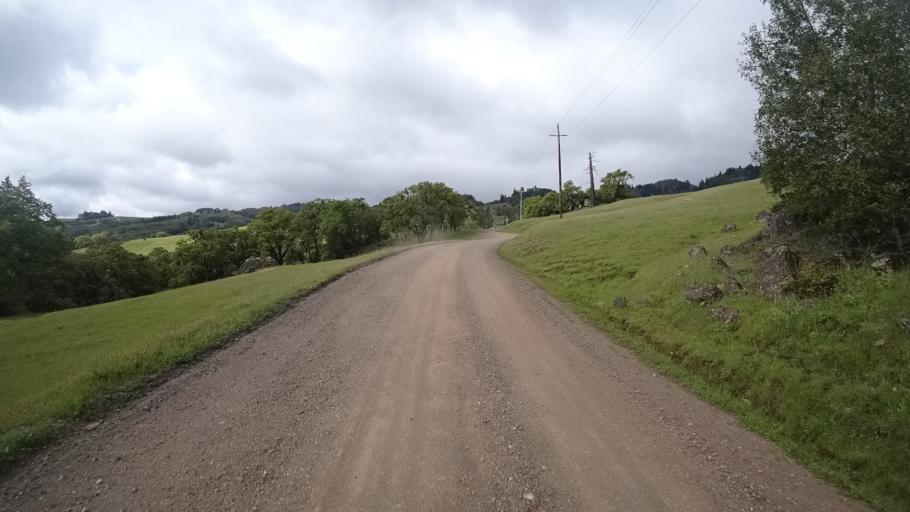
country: US
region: California
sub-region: Humboldt County
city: Redway
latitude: 40.2083
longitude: -123.6856
